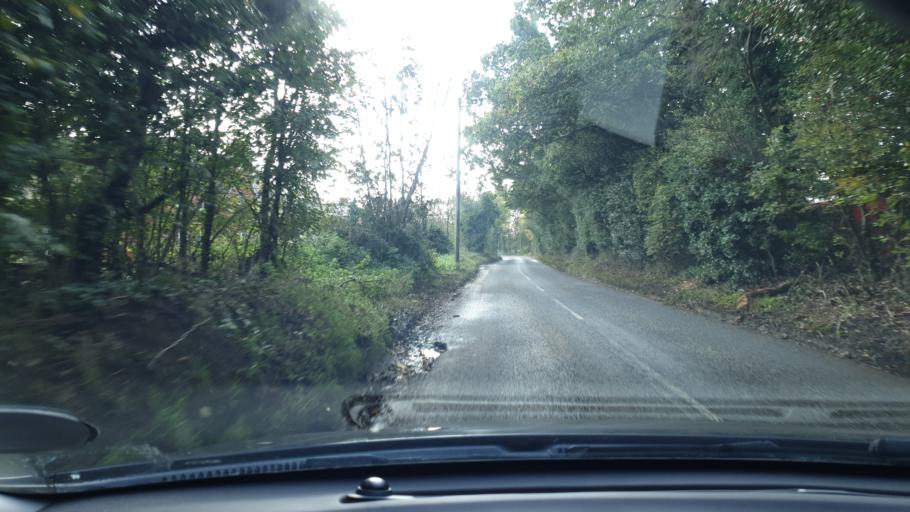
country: GB
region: England
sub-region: Essex
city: Manningtree
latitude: 51.9355
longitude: 1.0453
